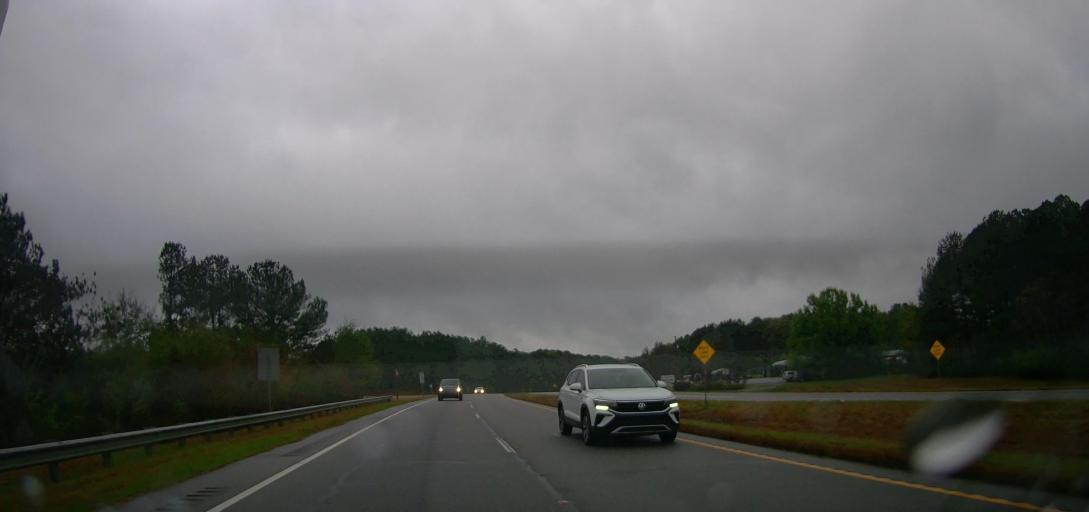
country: US
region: Georgia
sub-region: Oconee County
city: Watkinsville
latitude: 33.8470
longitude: -83.4222
